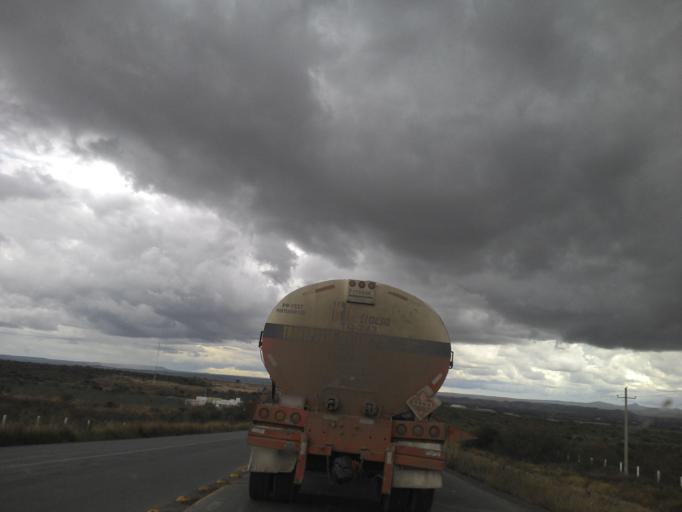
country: MX
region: Zacatecas
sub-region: Rio Grande
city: Los Condes
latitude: 23.8735
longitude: -103.0876
